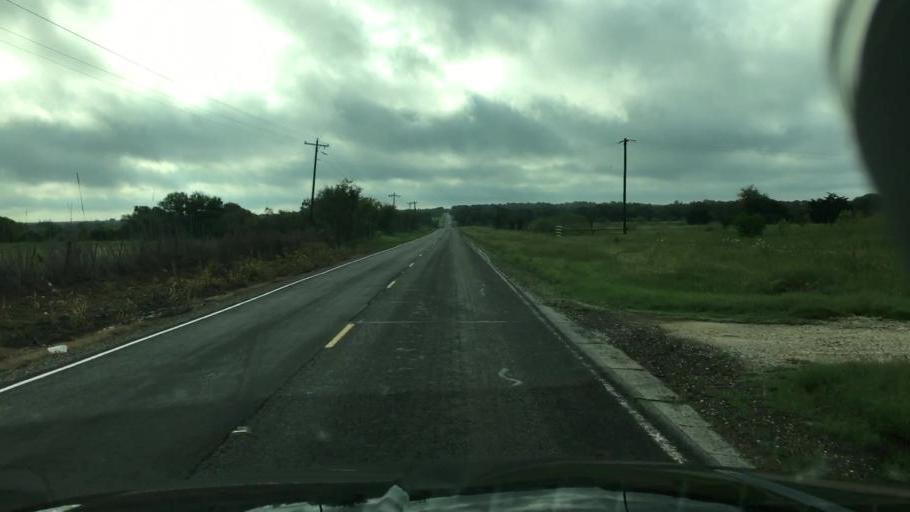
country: US
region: Texas
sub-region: Lee County
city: Lexington
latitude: 30.3749
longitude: -96.8469
